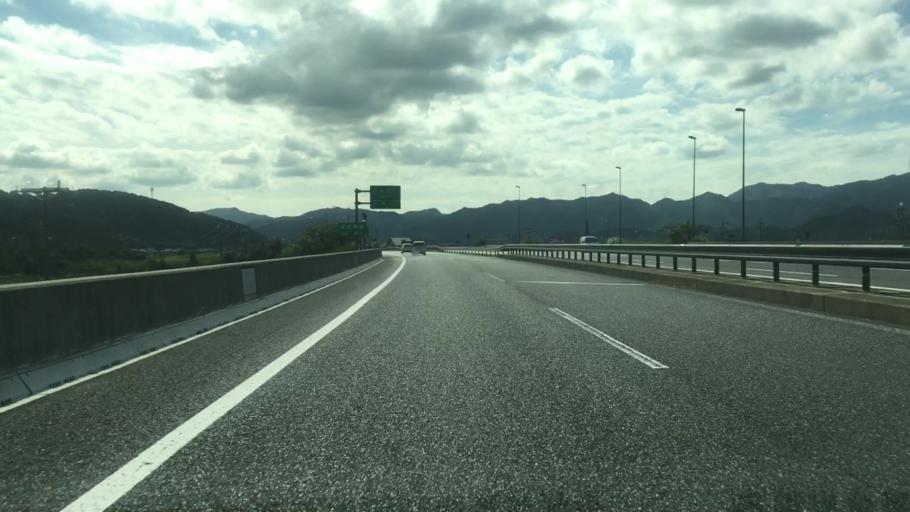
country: JP
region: Kyoto
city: Fukuchiyama
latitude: 35.1657
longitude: 135.0443
